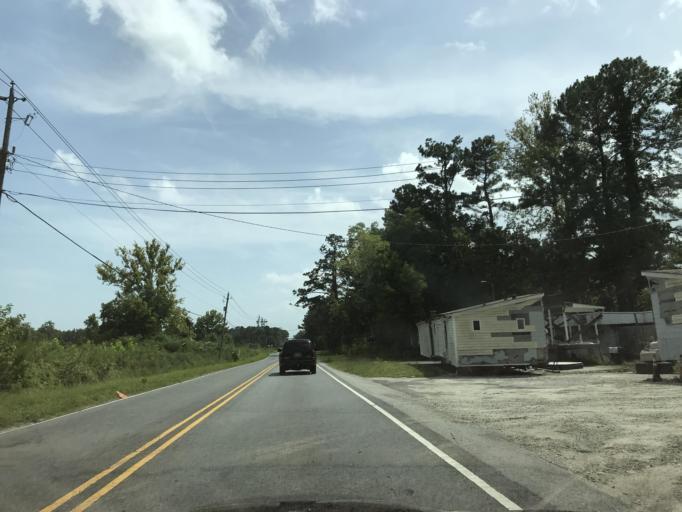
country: US
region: North Carolina
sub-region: New Hanover County
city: Wrightsboro
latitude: 34.3091
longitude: -77.9221
